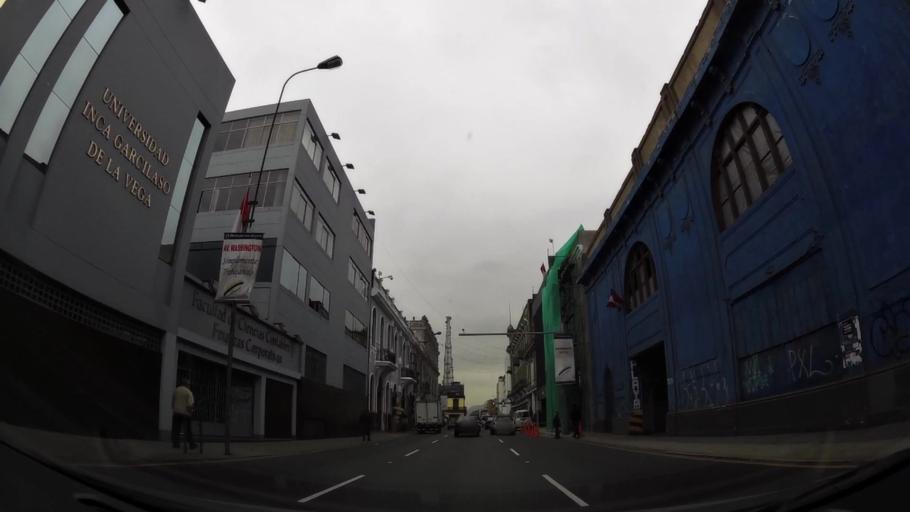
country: PE
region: Lima
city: Lima
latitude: -12.0610
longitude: -77.0390
